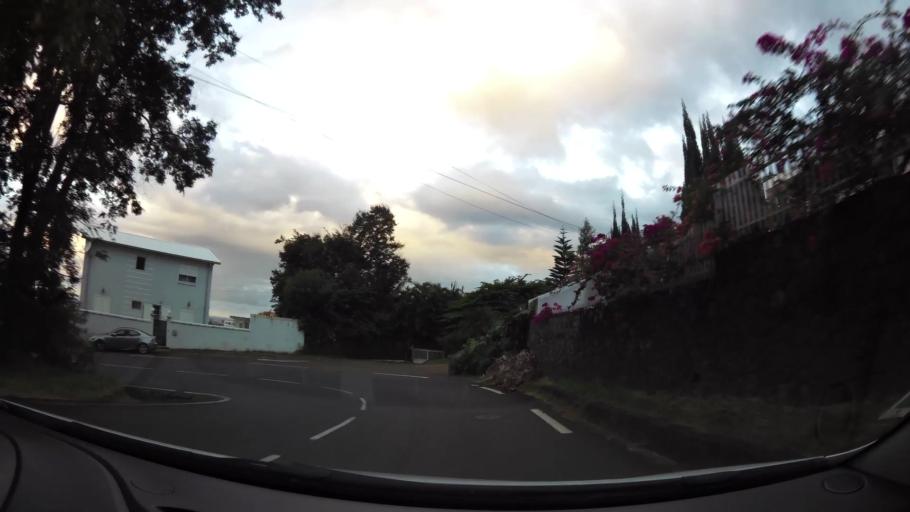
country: RE
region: Reunion
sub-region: Reunion
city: Saint-Denis
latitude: -20.9012
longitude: 55.4631
